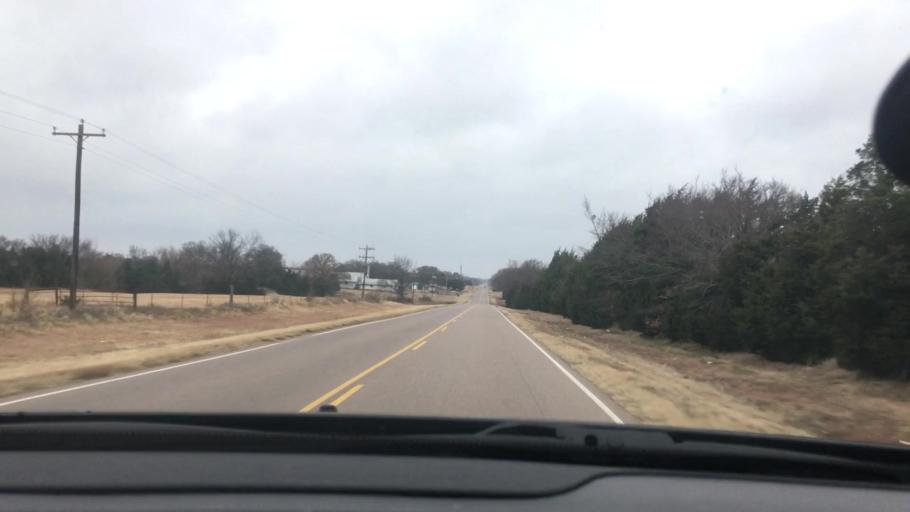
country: US
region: Oklahoma
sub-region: Johnston County
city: Tishomingo
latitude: 34.2784
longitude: -96.6711
